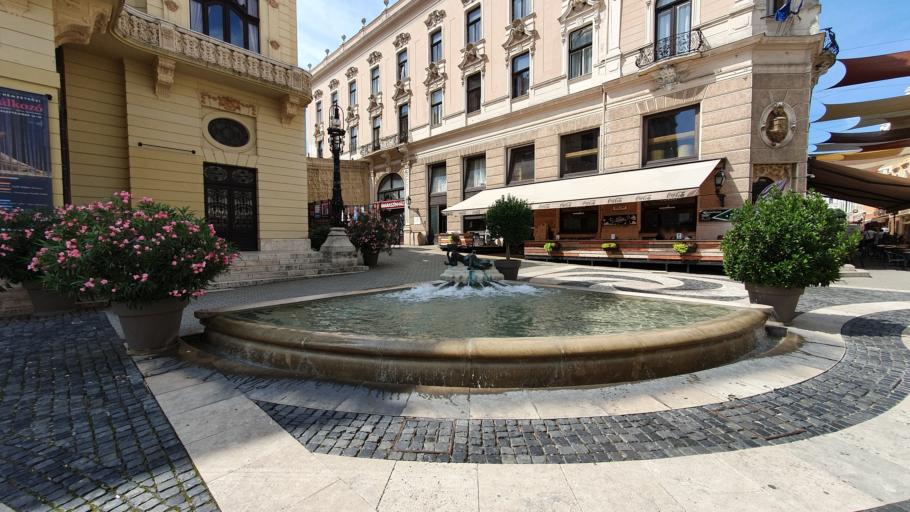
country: HU
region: Baranya
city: Pecs
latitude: 46.0766
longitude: 18.2304
